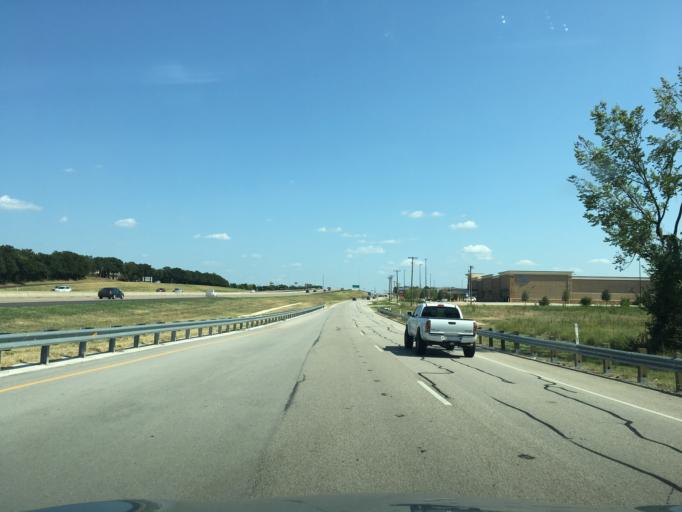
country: US
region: Texas
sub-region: Tarrant County
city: Kennedale
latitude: 32.6510
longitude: -97.1893
